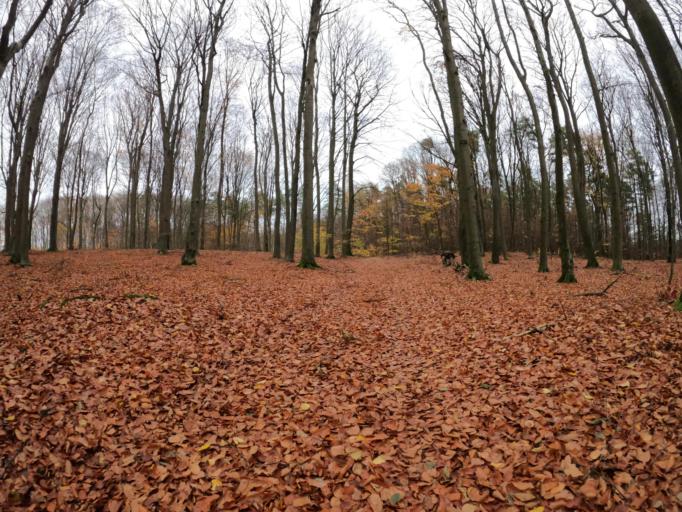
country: PL
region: West Pomeranian Voivodeship
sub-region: Powiat walecki
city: Tuczno
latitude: 53.2486
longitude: 16.2280
